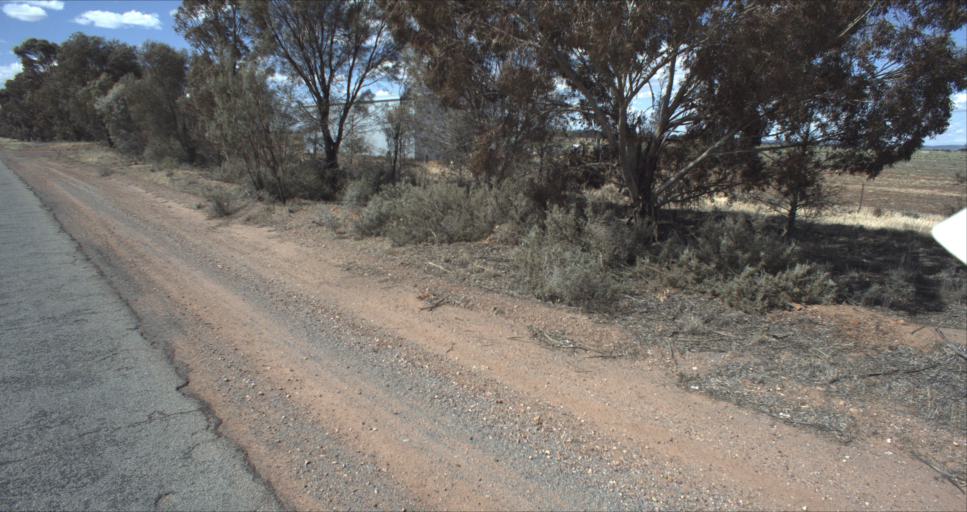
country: AU
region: New South Wales
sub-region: Leeton
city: Leeton
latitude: -34.4757
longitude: 146.2501
